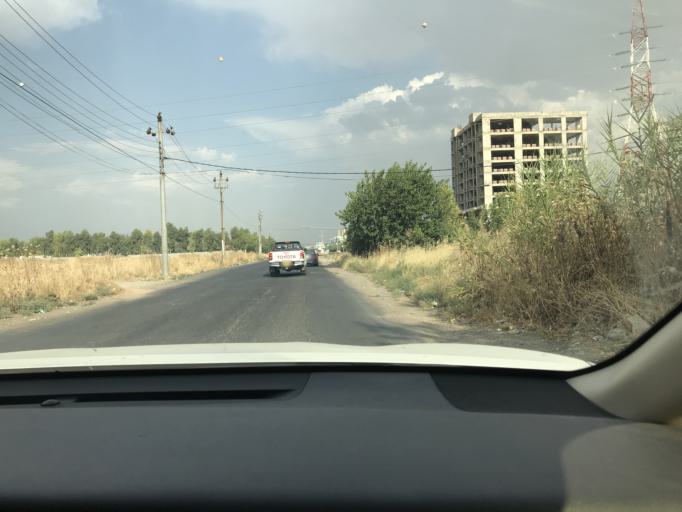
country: IQ
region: Arbil
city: Erbil
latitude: 36.2072
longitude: 43.9590
